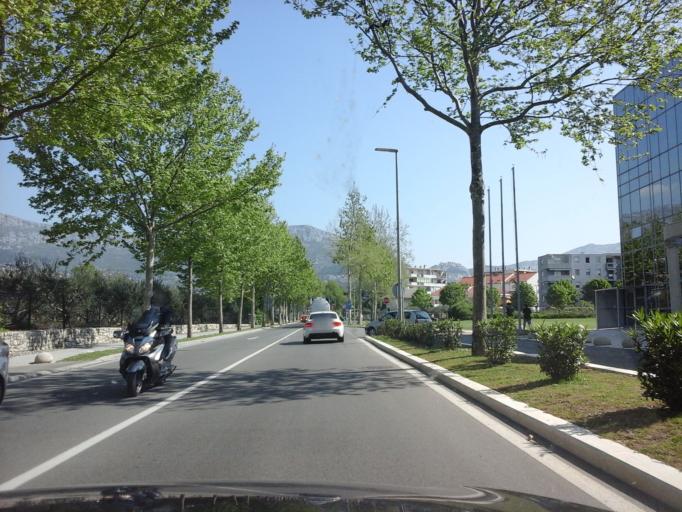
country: HR
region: Splitsko-Dalmatinska
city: Solin
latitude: 43.5379
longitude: 16.4884
